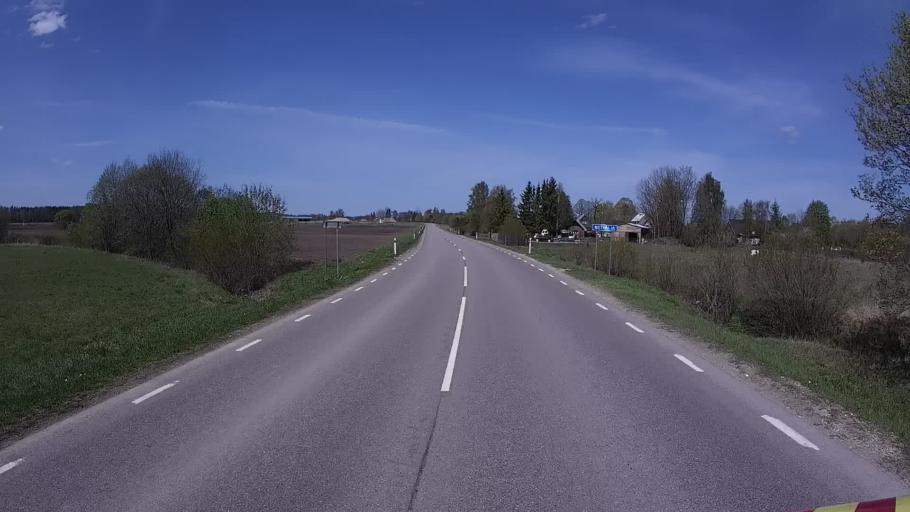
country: EE
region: Harju
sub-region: Keila linn
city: Keila
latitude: 59.3047
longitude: 24.3248
